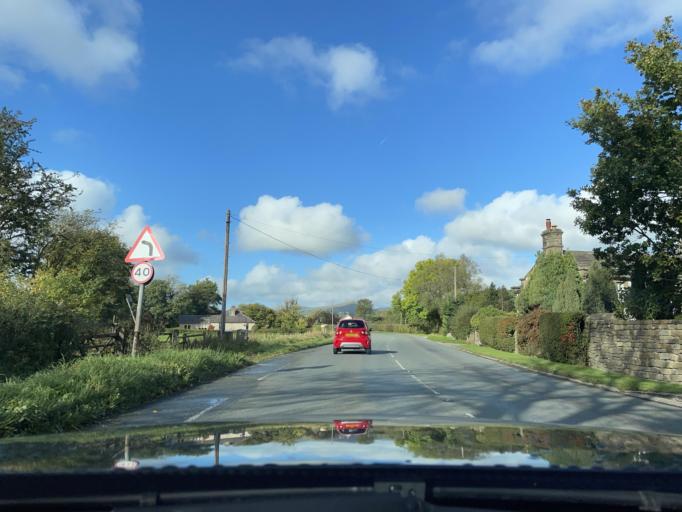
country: GB
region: England
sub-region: Derbyshire
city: Hope Valley
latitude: 53.3410
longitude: -1.6998
